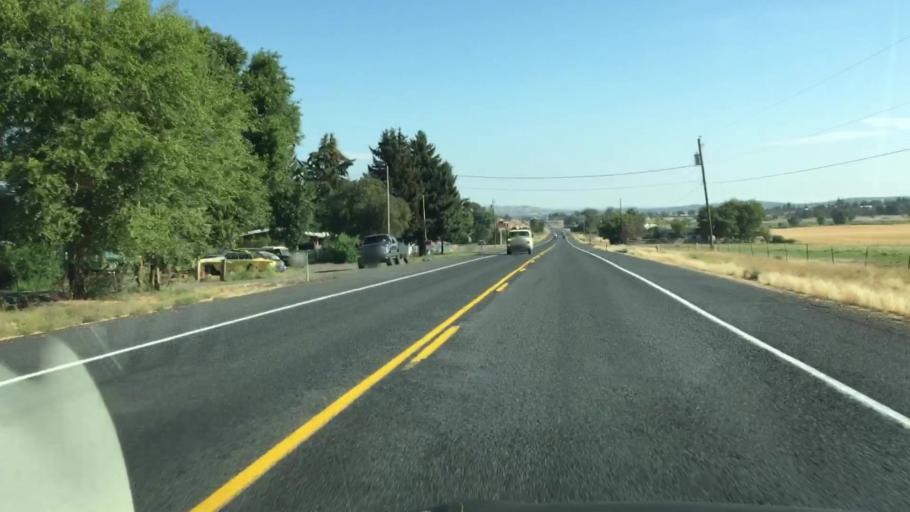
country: US
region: Oregon
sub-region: Jefferson County
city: Madras
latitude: 44.5944
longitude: -121.1463
